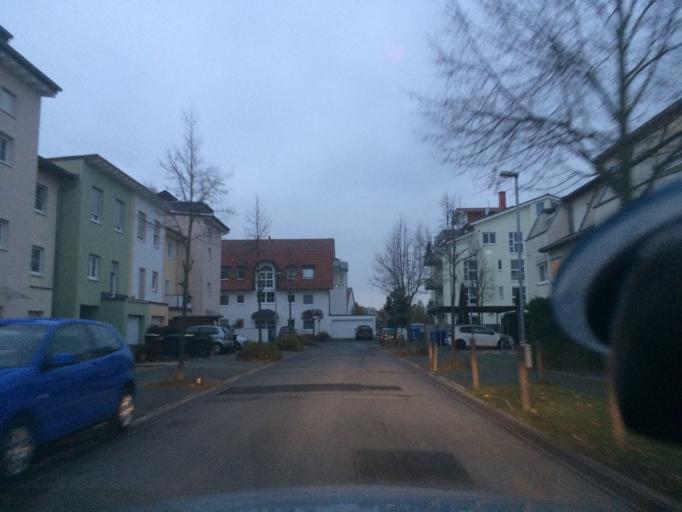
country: DE
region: Hesse
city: Morfelden-Walldorf
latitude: 49.9957
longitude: 8.5741
